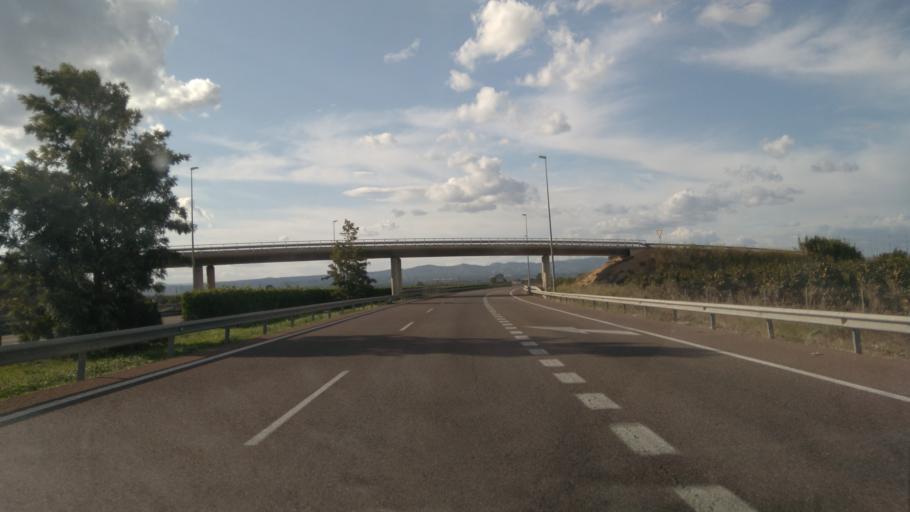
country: ES
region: Valencia
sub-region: Provincia de Valencia
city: Guadassuar
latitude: 39.1779
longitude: -0.4787
